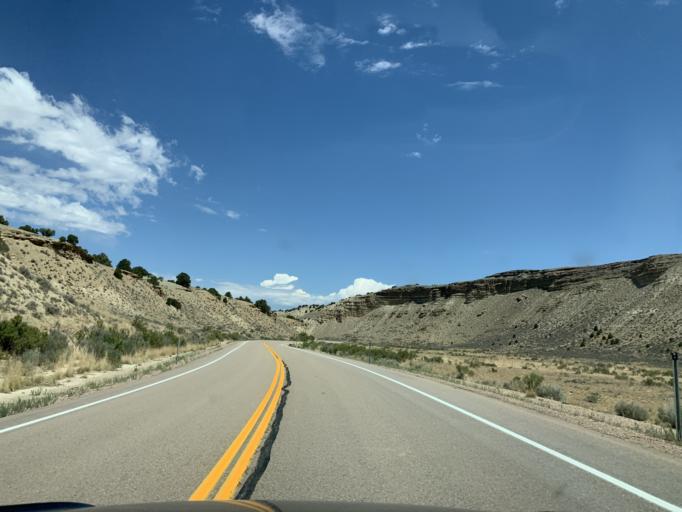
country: US
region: Utah
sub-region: Duchesne County
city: Duchesne
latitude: 39.9745
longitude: -110.1630
